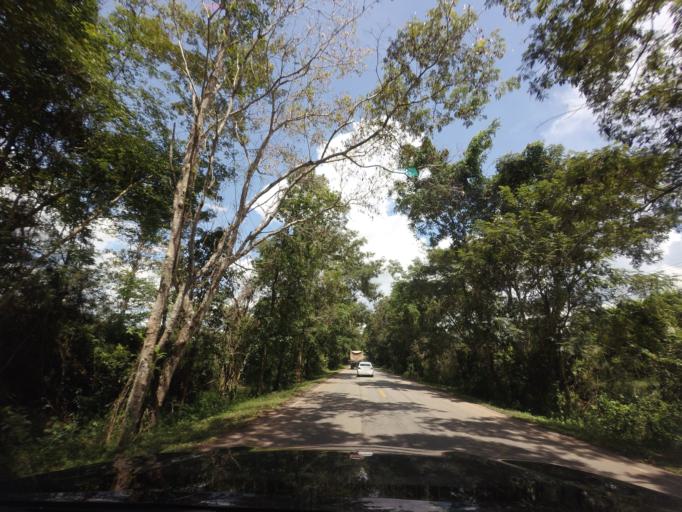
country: TH
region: Changwat Udon Thani
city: Phibun Rak
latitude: 17.5848
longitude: 103.0419
